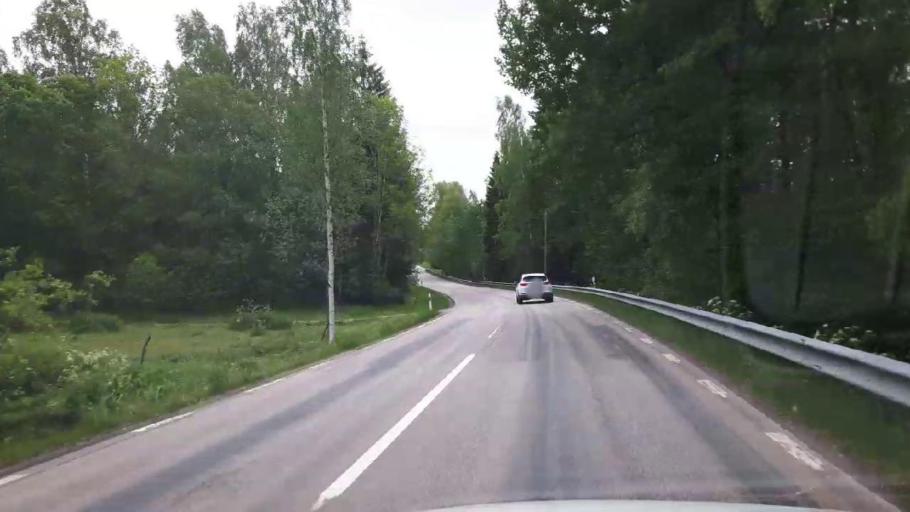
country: SE
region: Vaestmanland
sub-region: Norbergs Kommun
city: Norberg
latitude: 60.1109
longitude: 15.9193
